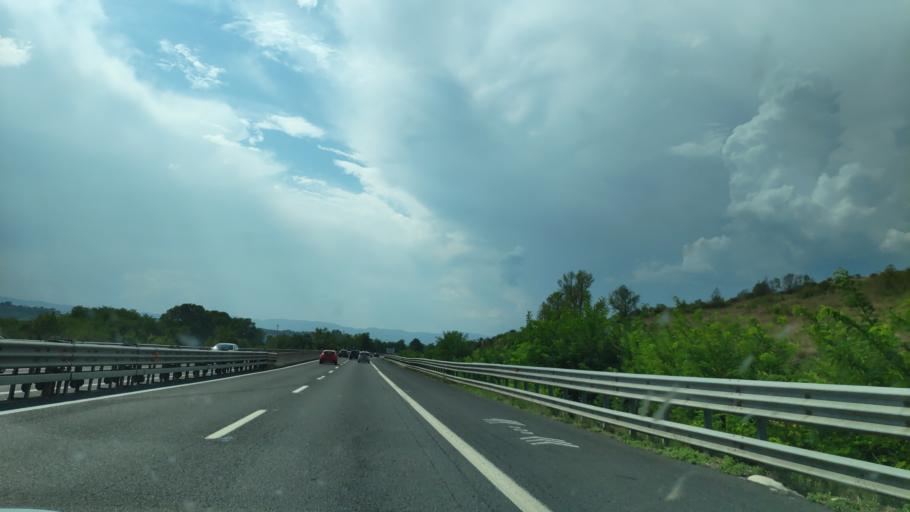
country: IT
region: Tuscany
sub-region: Province of Arezzo
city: Bucine
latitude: 43.5147
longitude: 11.6203
